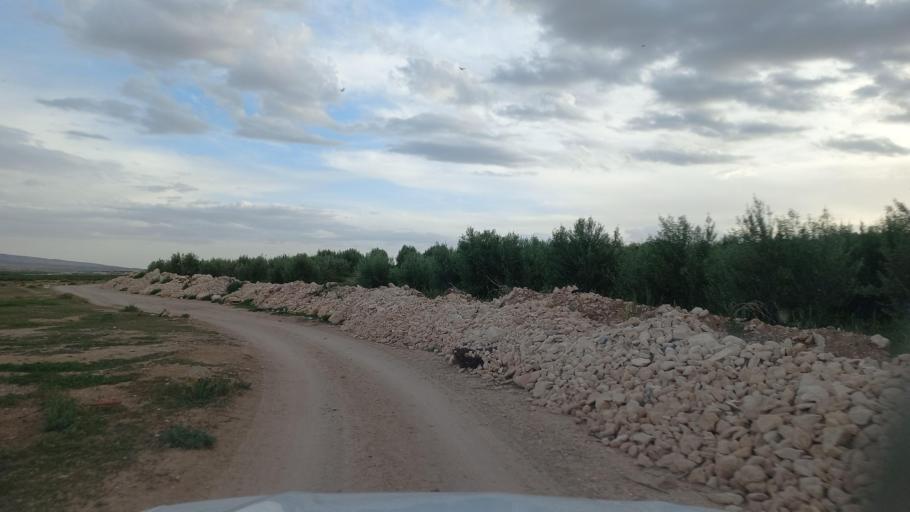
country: TN
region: Al Qasrayn
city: Sbiba
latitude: 35.4318
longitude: 9.0982
